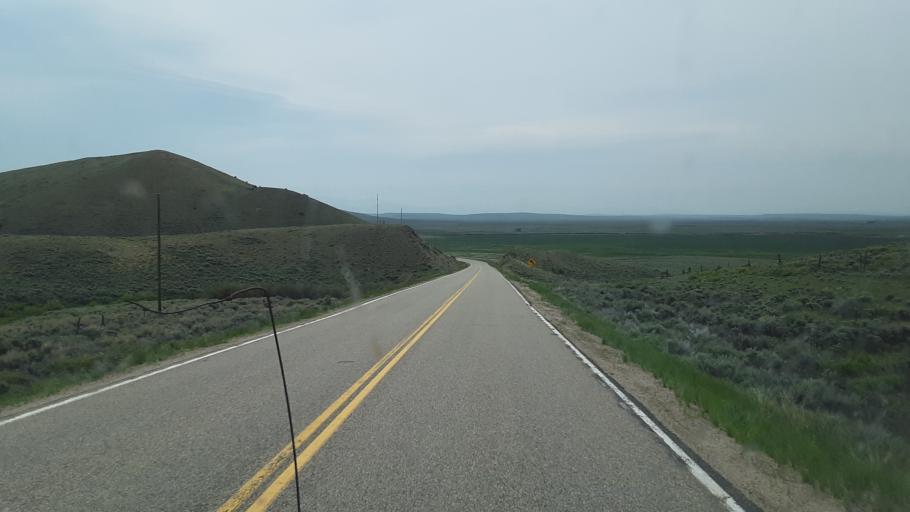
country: US
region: Colorado
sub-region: Jackson County
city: Walden
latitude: 40.9221
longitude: -106.3133
